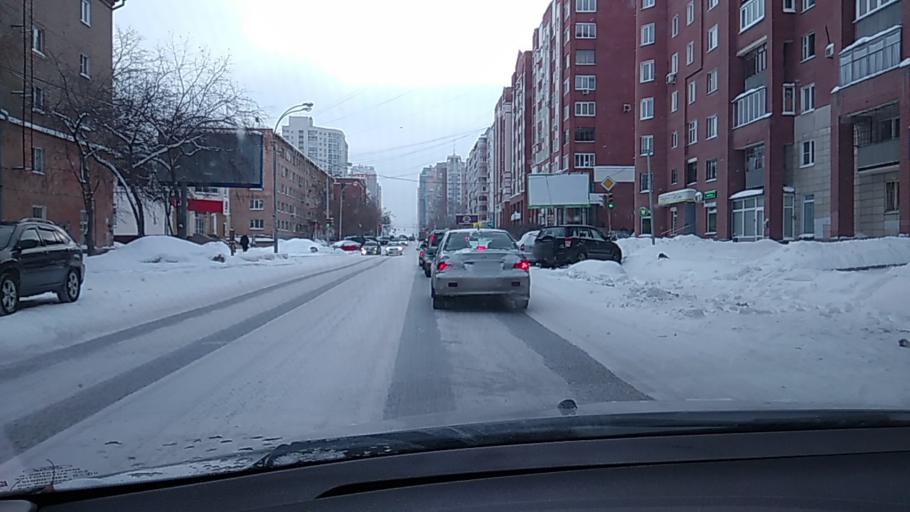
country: RU
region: Sverdlovsk
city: Yekaterinburg
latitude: 56.8105
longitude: 60.6005
